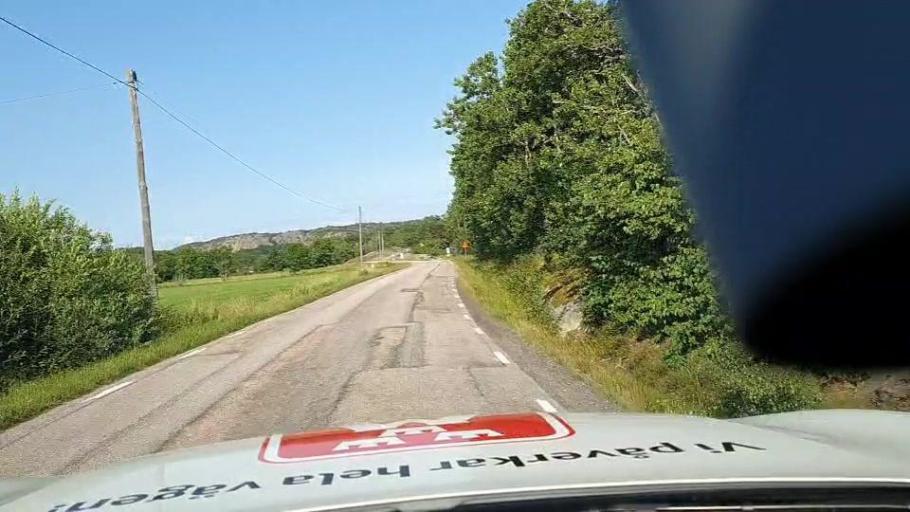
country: SE
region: Vaestra Goetaland
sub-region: Lysekils Kommun
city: Lysekil
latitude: 58.1340
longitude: 11.4531
